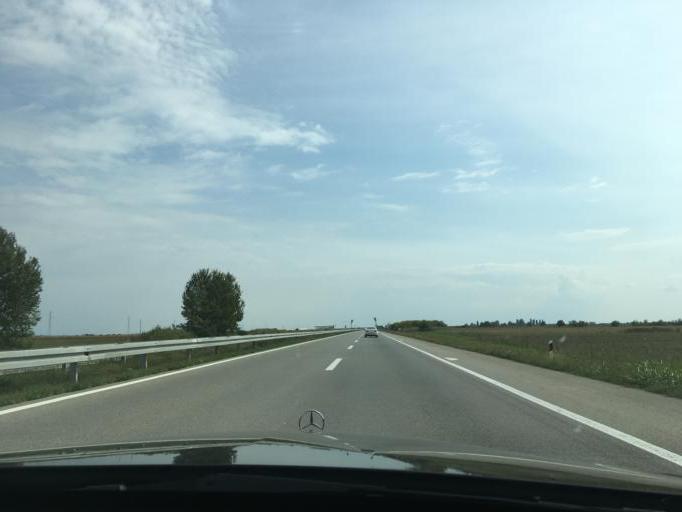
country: RS
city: Ravnje
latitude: 45.0392
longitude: 19.4397
